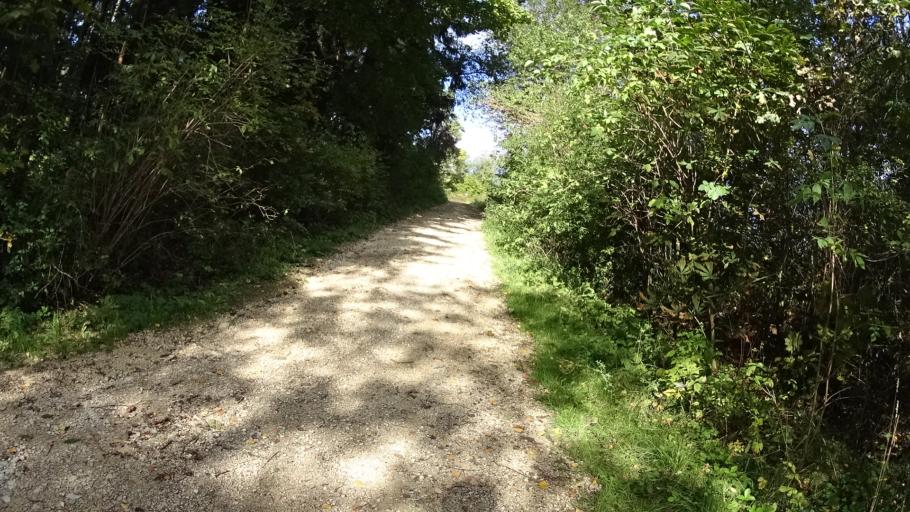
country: DE
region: Bavaria
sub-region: Upper Bavaria
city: Bohmfeld
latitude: 48.8463
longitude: 11.3704
